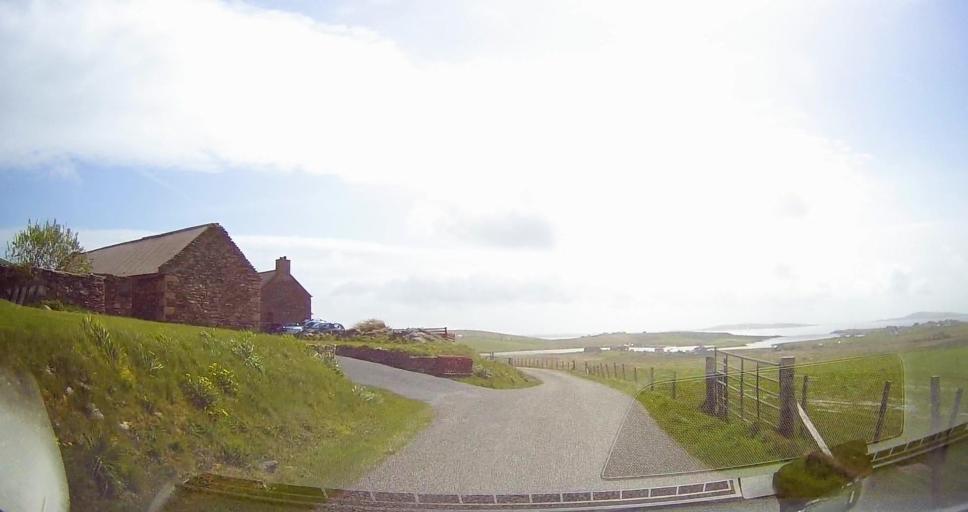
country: GB
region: Scotland
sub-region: Shetland Islands
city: Sandwick
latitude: 60.0502
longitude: -1.2212
